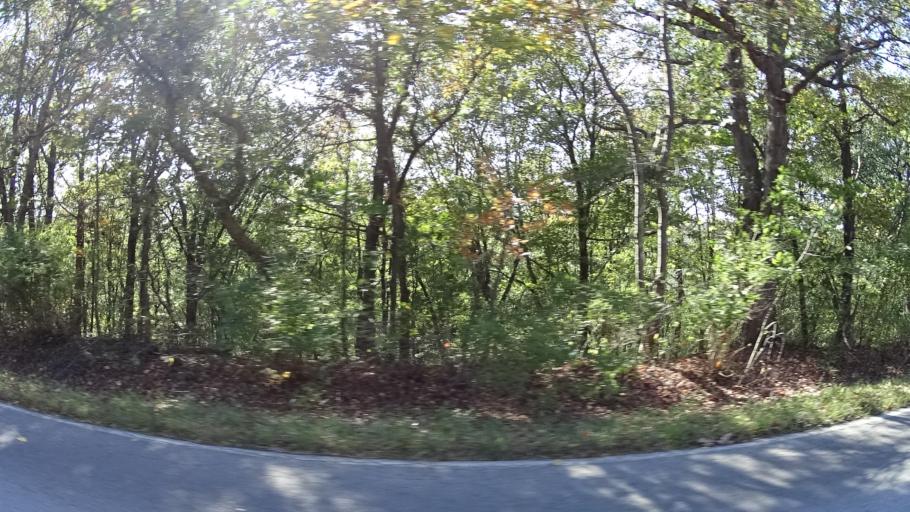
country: US
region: Ohio
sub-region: Lorain County
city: Vermilion-on-the-Lake
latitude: 41.4068
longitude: -82.3294
